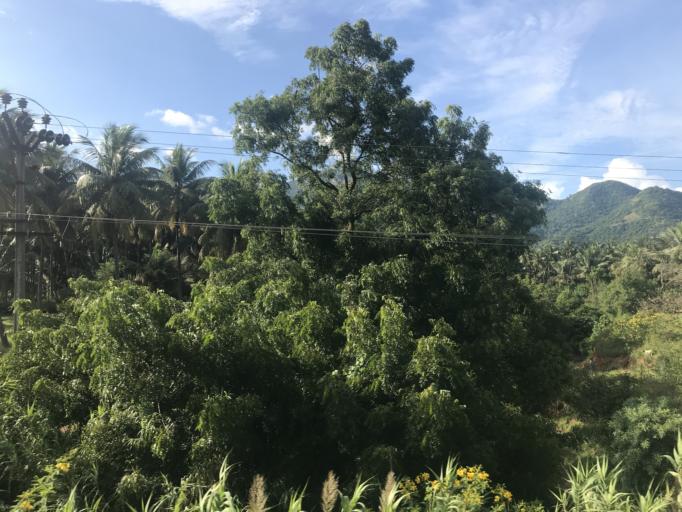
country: IN
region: Tamil Nadu
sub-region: Coimbatore
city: Madukkarai
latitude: 10.8828
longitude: 76.8691
